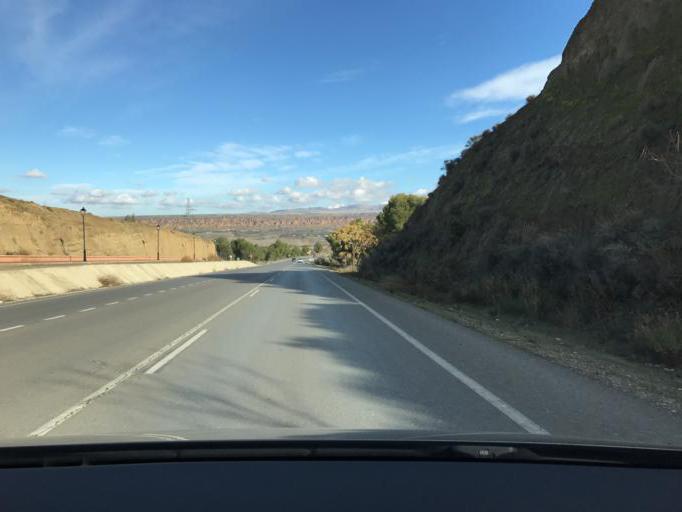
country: ES
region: Andalusia
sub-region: Provincia de Granada
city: Purullena
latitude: 37.3186
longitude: -3.1772
